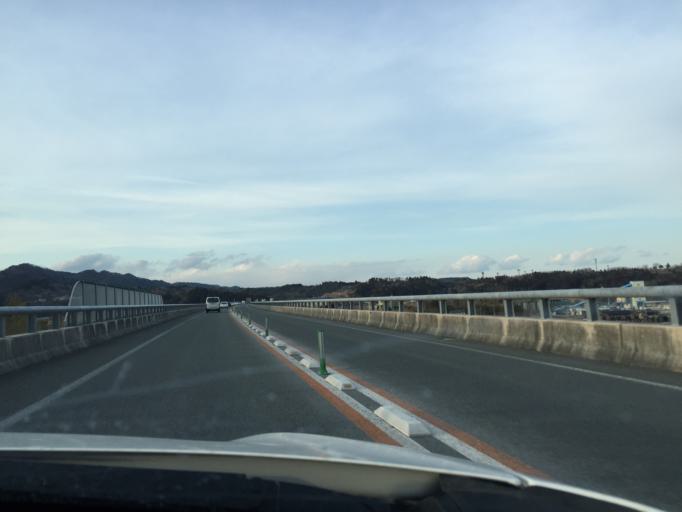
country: JP
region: Fukushima
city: Namie
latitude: 37.2725
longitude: 140.9835
